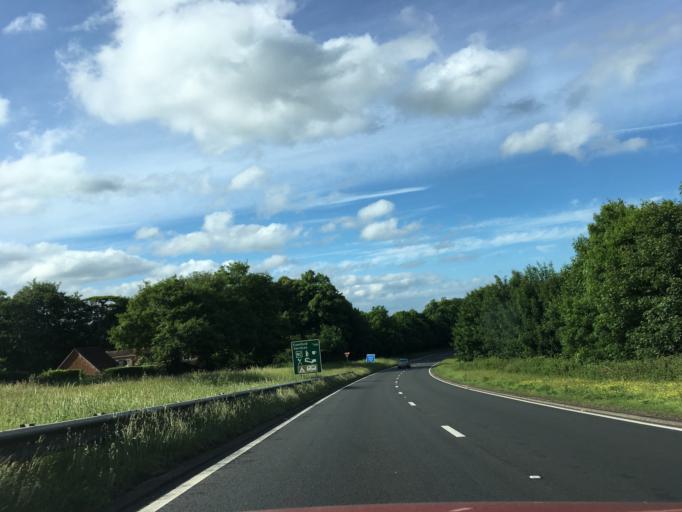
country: GB
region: England
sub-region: Devon
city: Exminster
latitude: 50.6514
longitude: -3.5448
